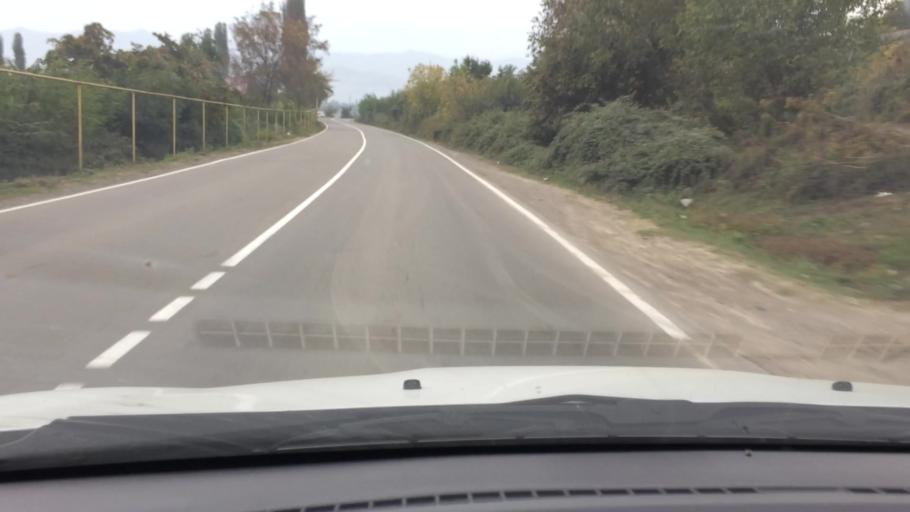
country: AM
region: Tavush
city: Bagratashen
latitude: 41.2786
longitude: 44.7908
